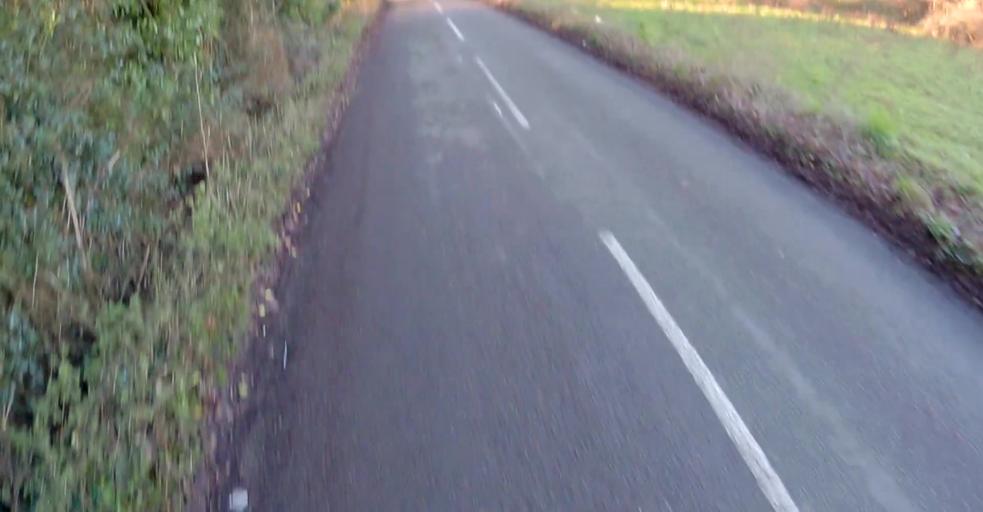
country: GB
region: England
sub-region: Hampshire
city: Hook
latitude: 51.2945
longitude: -0.9772
